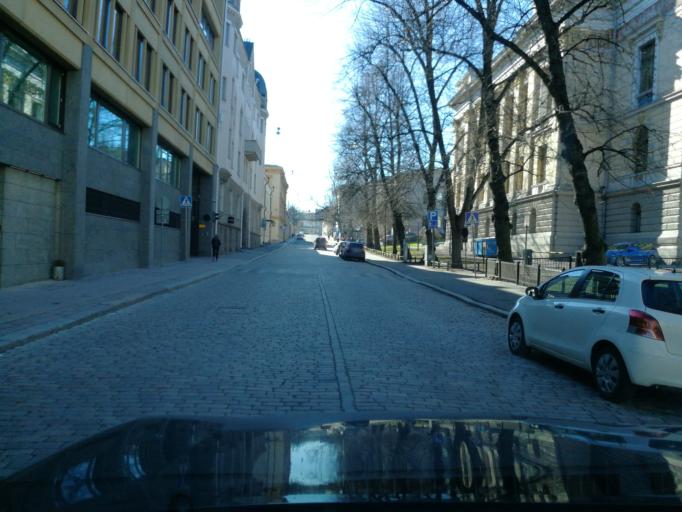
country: FI
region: Uusimaa
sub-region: Helsinki
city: Helsinki
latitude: 60.1709
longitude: 24.9554
